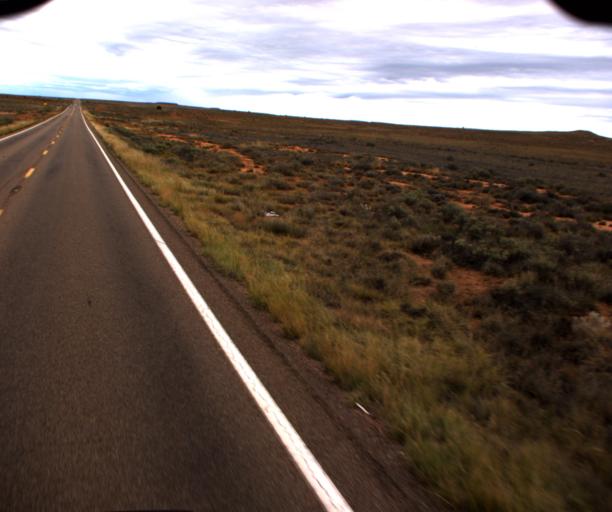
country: US
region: Arizona
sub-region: Navajo County
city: Holbrook
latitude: 34.7782
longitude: -110.1294
